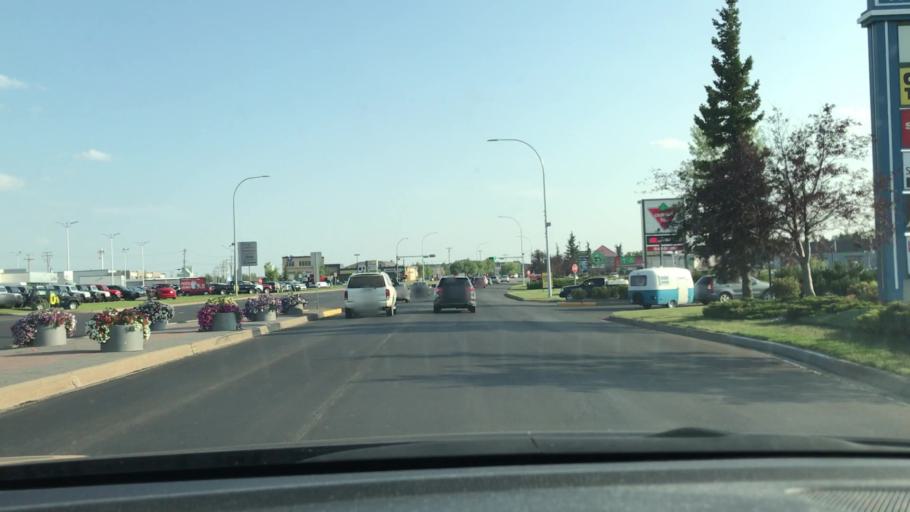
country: CA
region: Alberta
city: Leduc
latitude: 53.2763
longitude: -113.5488
